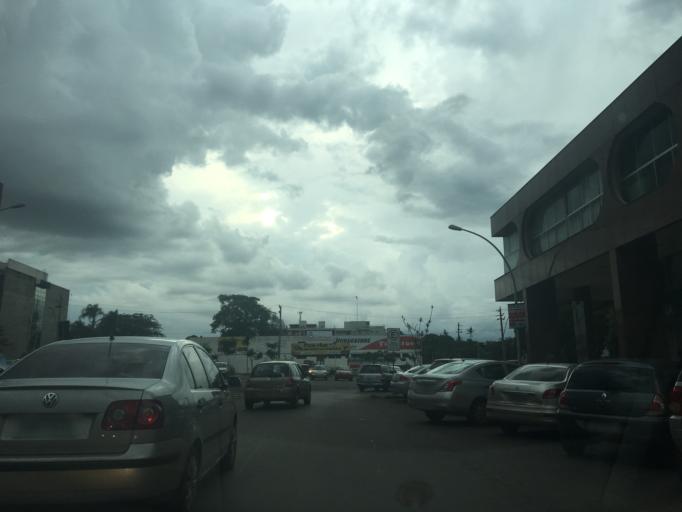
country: BR
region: Federal District
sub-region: Brasilia
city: Brasilia
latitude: -15.7442
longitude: -47.8955
